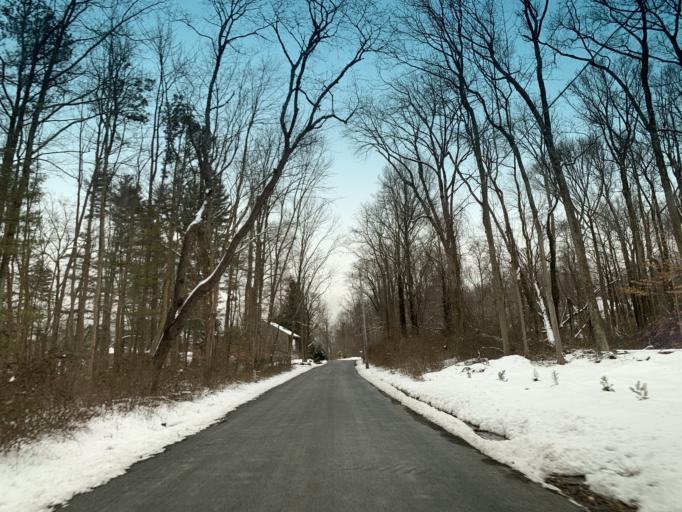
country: US
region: Maryland
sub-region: Harford County
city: Aberdeen
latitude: 39.5614
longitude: -76.1827
